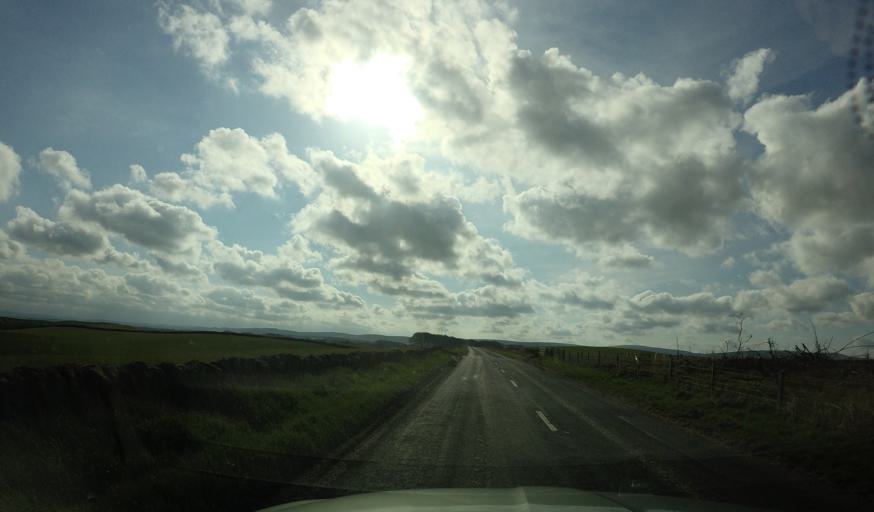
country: GB
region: Scotland
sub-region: Midlothian
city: Penicuik
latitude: 55.8069
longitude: -3.1794
